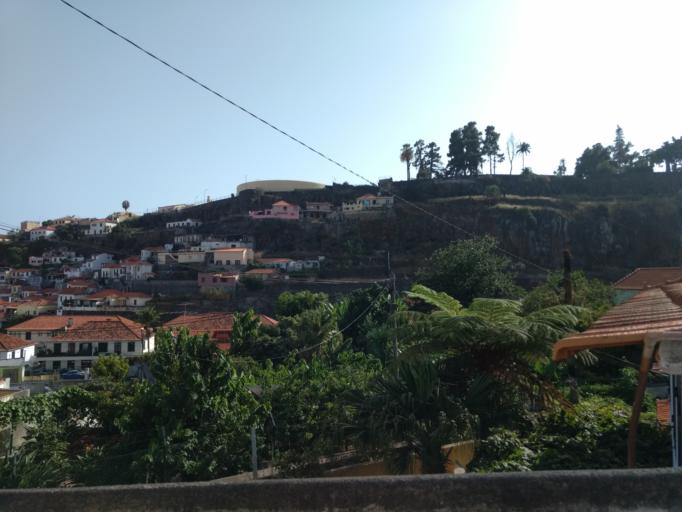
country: PT
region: Madeira
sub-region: Funchal
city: Nossa Senhora do Monte
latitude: 32.6569
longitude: -16.9152
